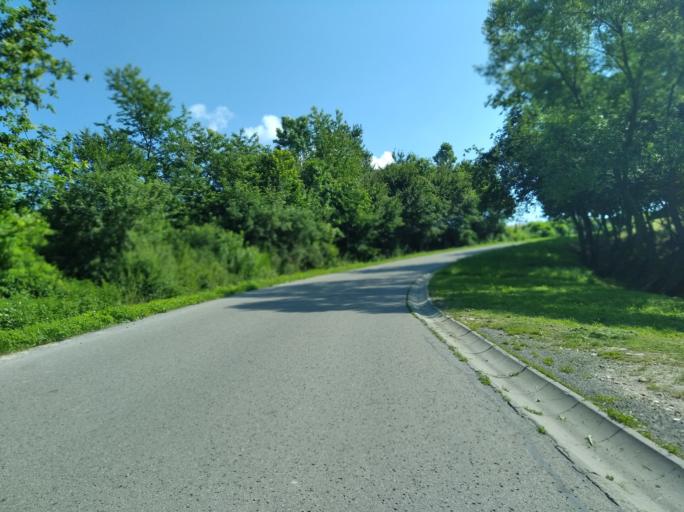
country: PL
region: Subcarpathian Voivodeship
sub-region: Powiat brzozowski
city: Nozdrzec
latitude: 49.8204
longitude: 22.1693
